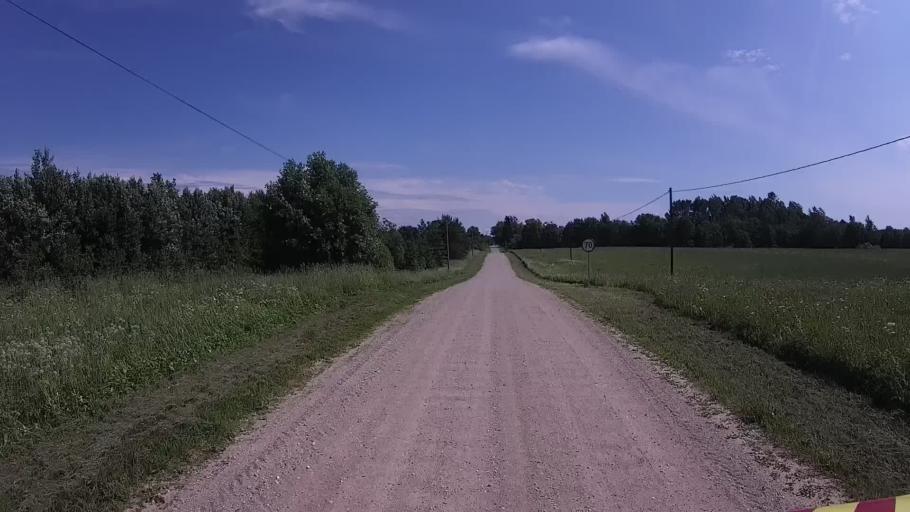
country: EE
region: Viljandimaa
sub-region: Karksi vald
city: Karksi-Nuia
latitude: 57.9972
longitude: 25.5323
